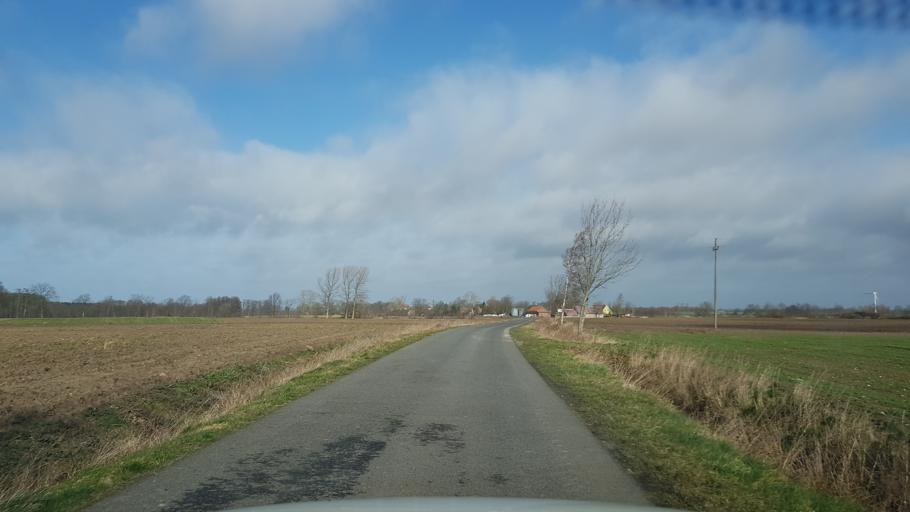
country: PL
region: West Pomeranian Voivodeship
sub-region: Powiat slawienski
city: Slawno
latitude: 54.5054
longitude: 16.6520
